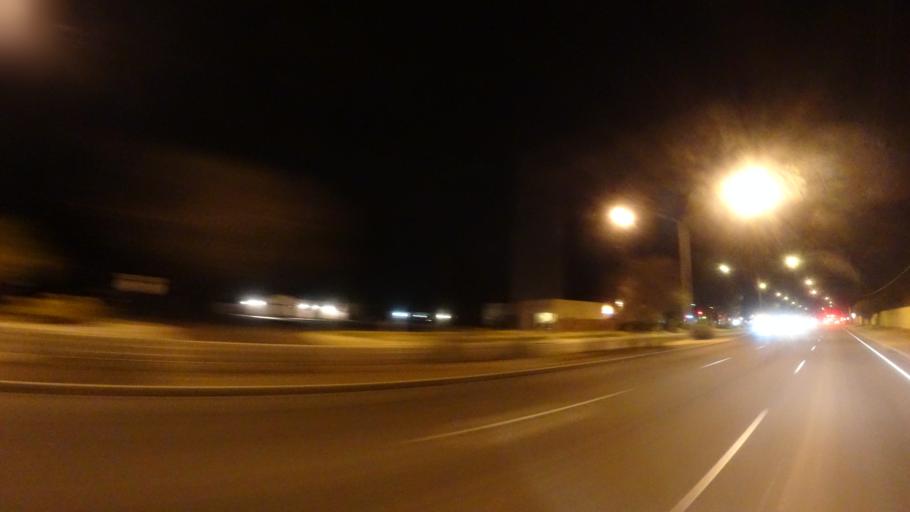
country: US
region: Arizona
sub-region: Maricopa County
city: Gilbert
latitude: 33.3976
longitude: -111.6847
